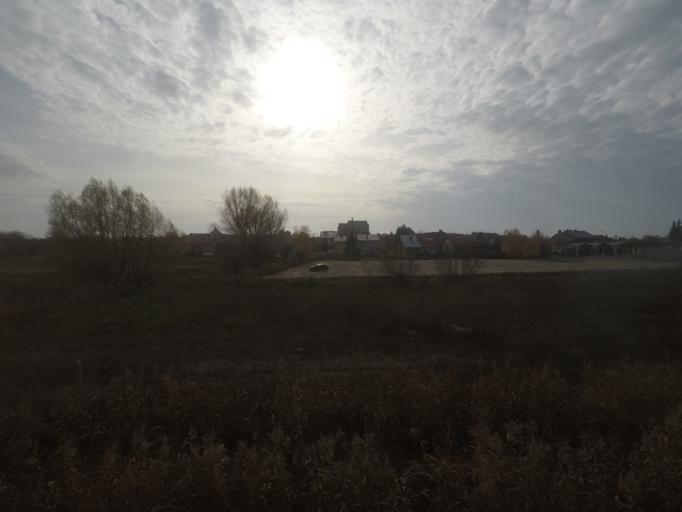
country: PL
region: Subcarpathian Voivodeship
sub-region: Powiat ropczycko-sedziszowski
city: Sedziszow Malopolski
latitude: 50.0749
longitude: 21.7031
